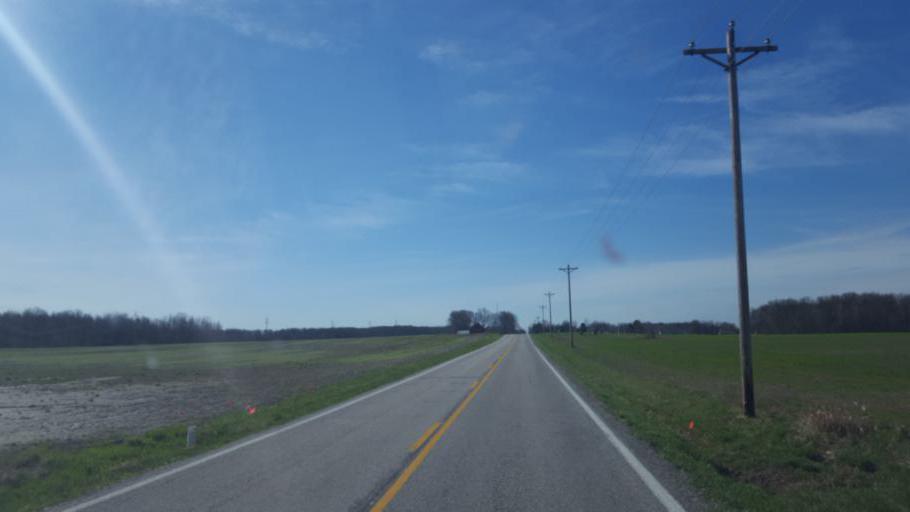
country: US
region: Ohio
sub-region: Morrow County
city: Cardington
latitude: 40.5654
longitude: -82.9623
